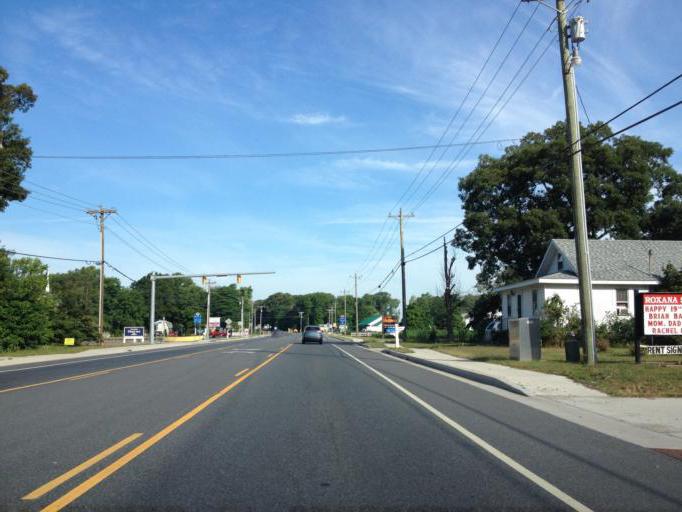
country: US
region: Delaware
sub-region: Sussex County
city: Ocean View
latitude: 38.4721
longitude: -75.0979
